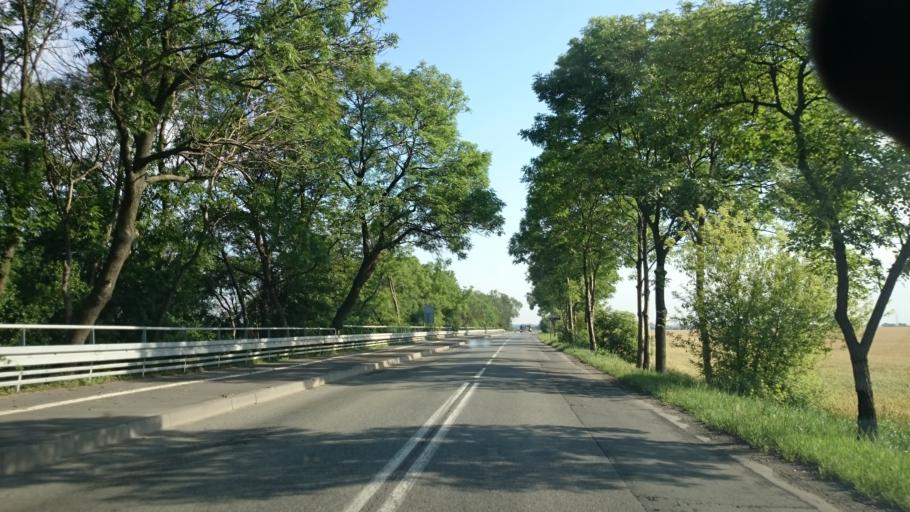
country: PL
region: Opole Voivodeship
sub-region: Powiat opolski
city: Opole
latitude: 50.6945
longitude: 17.9281
